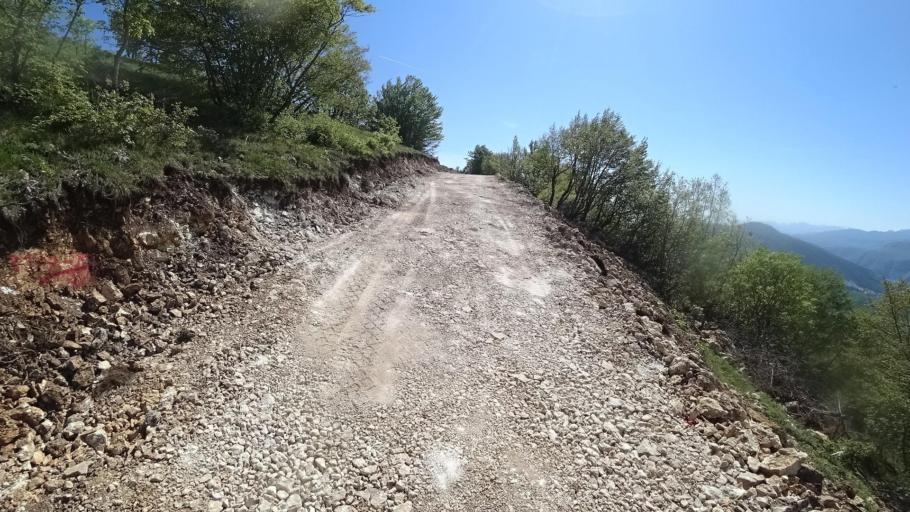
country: BA
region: Federation of Bosnia and Herzegovina
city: Rumboci
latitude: 43.8447
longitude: 17.5264
